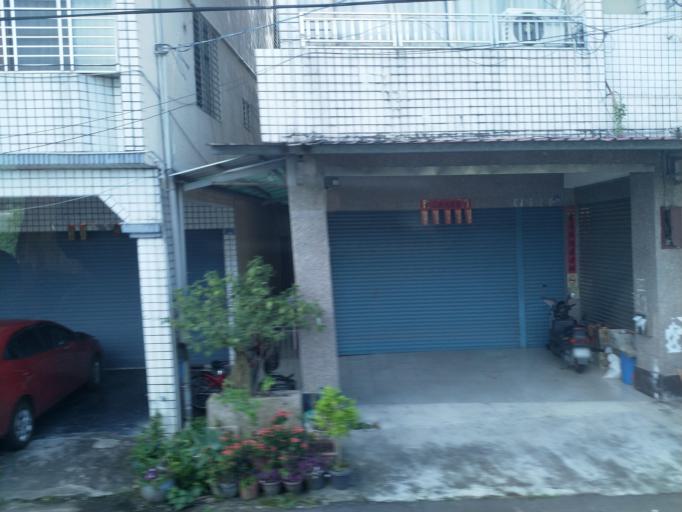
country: TW
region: Taiwan
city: Yujing
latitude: 22.9041
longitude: 120.5483
